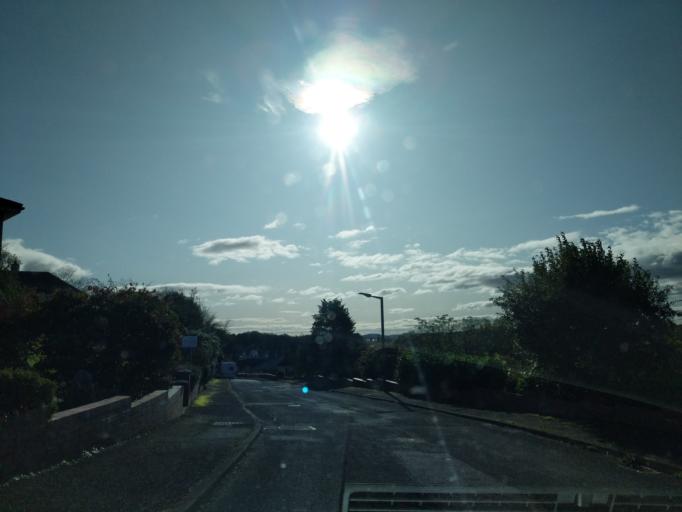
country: GB
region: Scotland
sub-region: Dumfries and Galloway
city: Kirkcudbright
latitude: 54.8319
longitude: -4.0495
